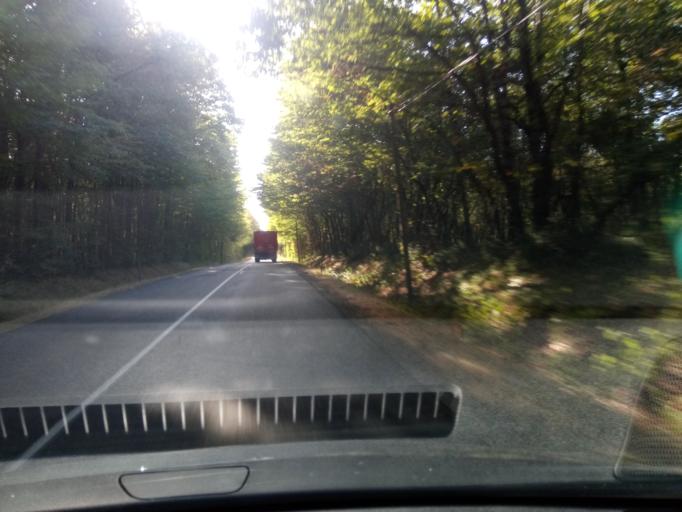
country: FR
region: Poitou-Charentes
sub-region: Departement de la Vienne
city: Montmorillon
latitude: 46.4423
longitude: 0.9557
